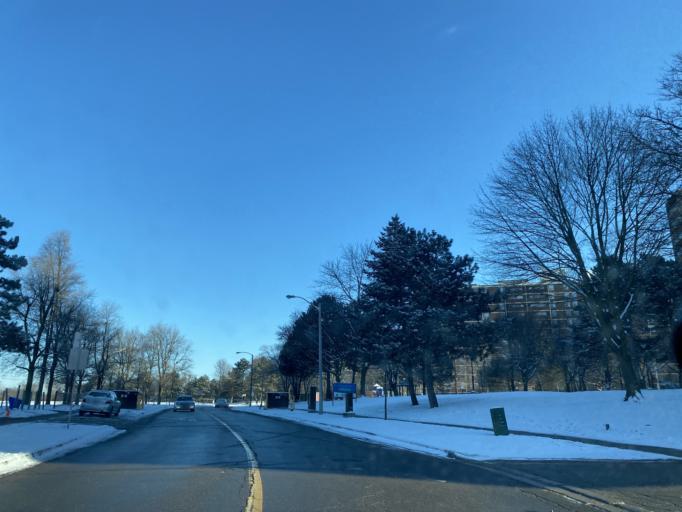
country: CA
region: Ontario
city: Scarborough
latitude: 43.7825
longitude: -79.3017
